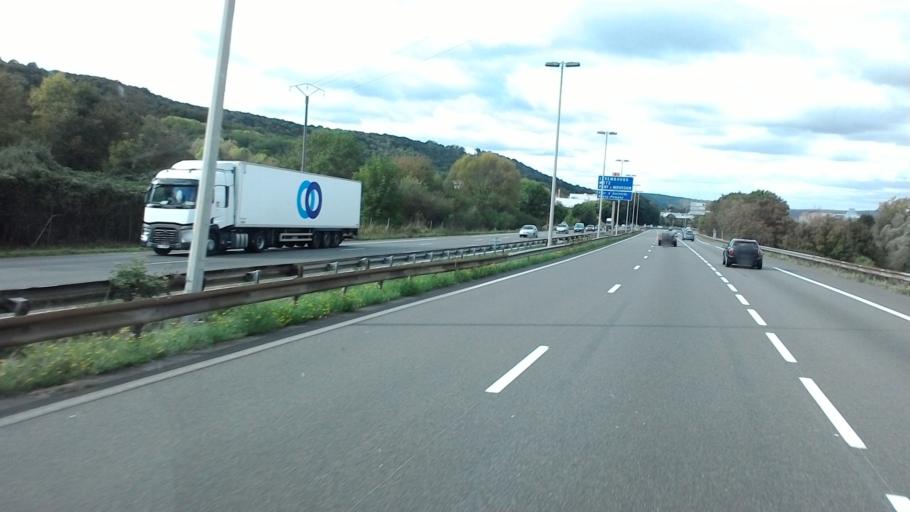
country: FR
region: Lorraine
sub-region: Departement de Meurthe-et-Moselle
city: Champigneulles
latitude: 48.7369
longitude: 6.1566
